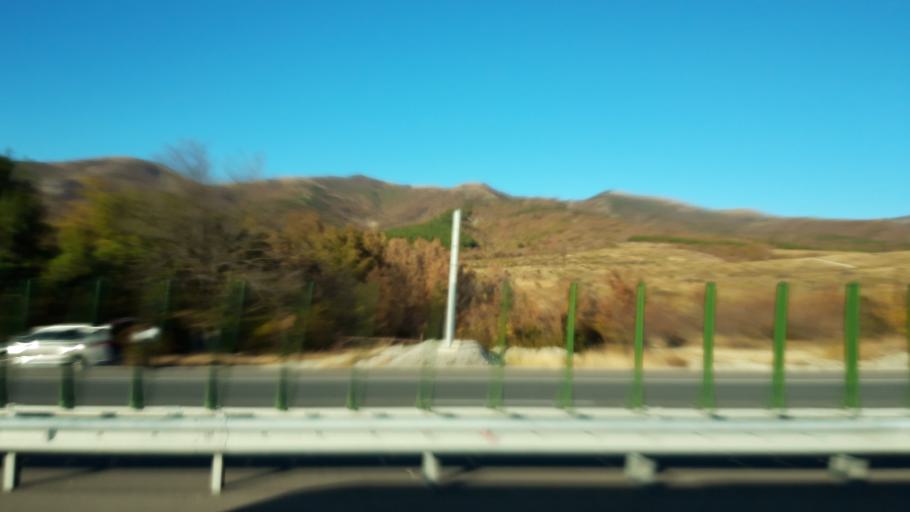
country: RU
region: Krasnodarskiy
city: Kabardinka
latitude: 44.6425
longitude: 37.9728
